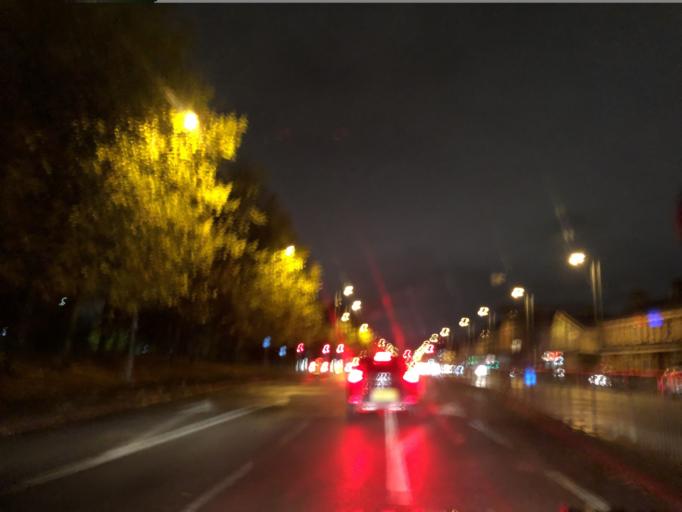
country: GB
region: England
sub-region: Manchester
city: Hulme
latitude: 53.4524
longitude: -2.2451
